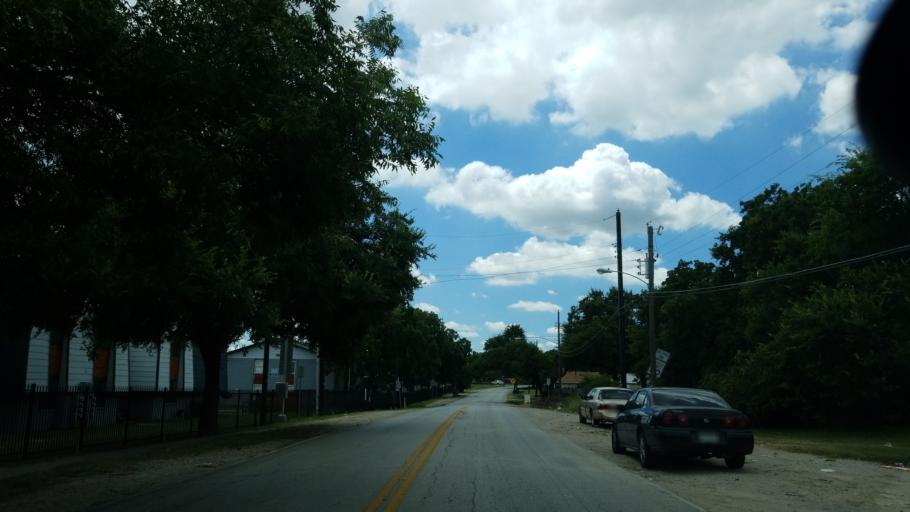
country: US
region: Texas
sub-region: Dallas County
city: Dallas
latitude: 32.7208
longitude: -96.7688
